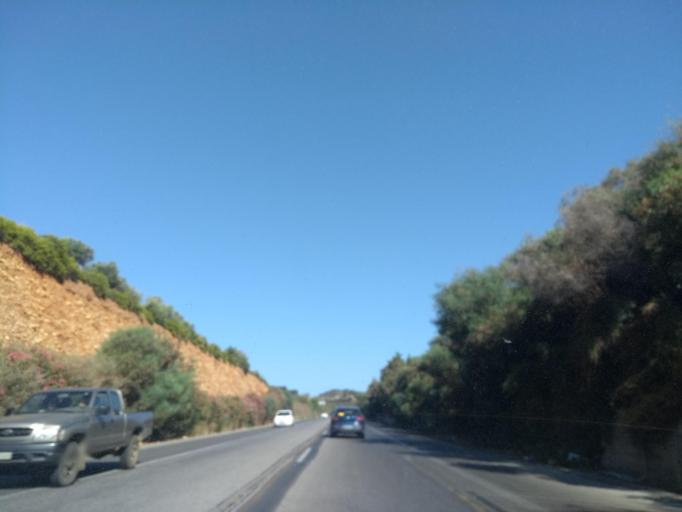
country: GR
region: Crete
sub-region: Nomos Chanias
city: Gerani
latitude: 35.5167
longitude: 23.8253
